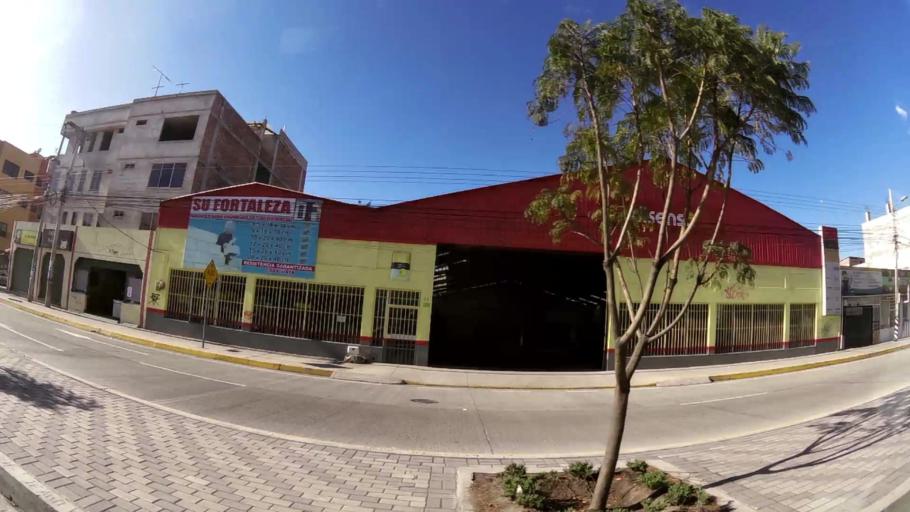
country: EC
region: Chimborazo
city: Riobamba
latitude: -1.6610
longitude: -78.6784
